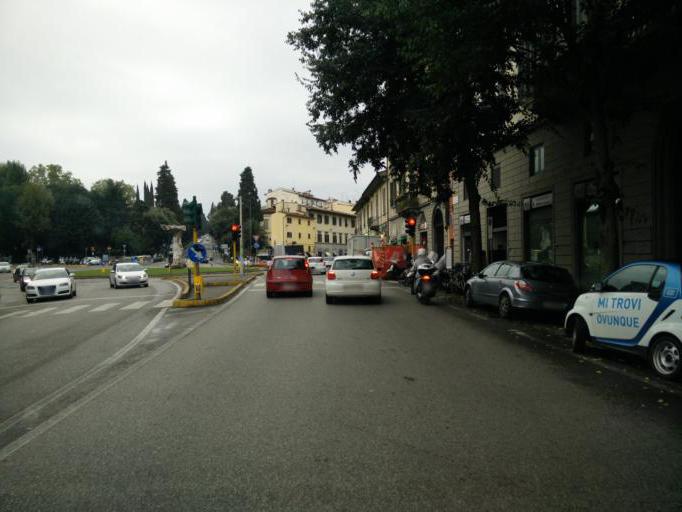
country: IT
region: Tuscany
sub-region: Province of Florence
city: Florence
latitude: 43.7611
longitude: 11.2413
